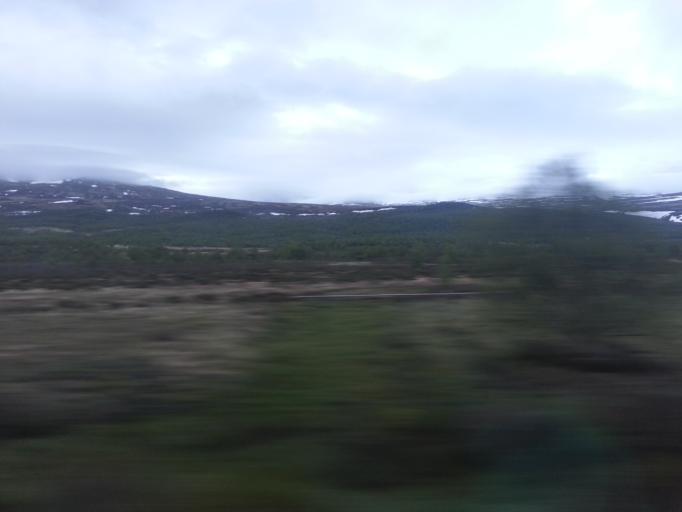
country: NO
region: Oppland
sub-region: Dovre
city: Dovre
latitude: 62.1228
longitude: 9.2816
